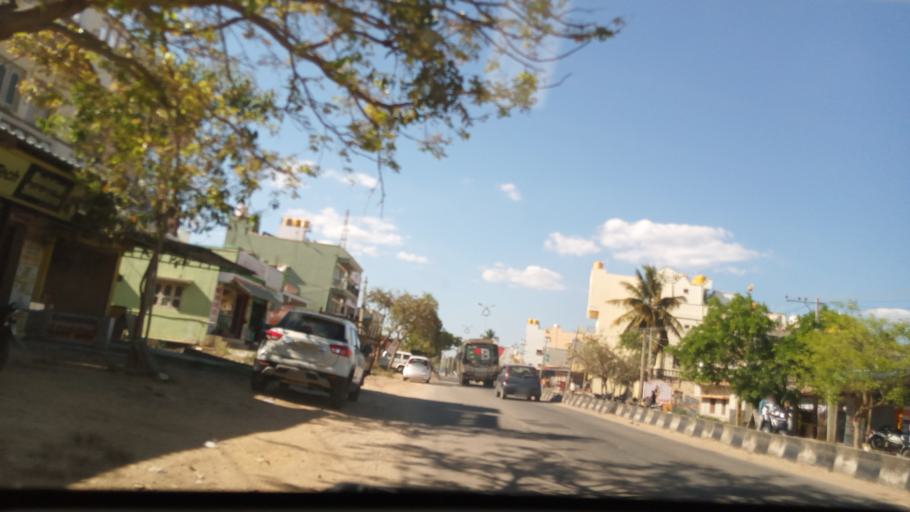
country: IN
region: Karnataka
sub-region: Kolar
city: Kolar
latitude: 13.1202
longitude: 78.1356
